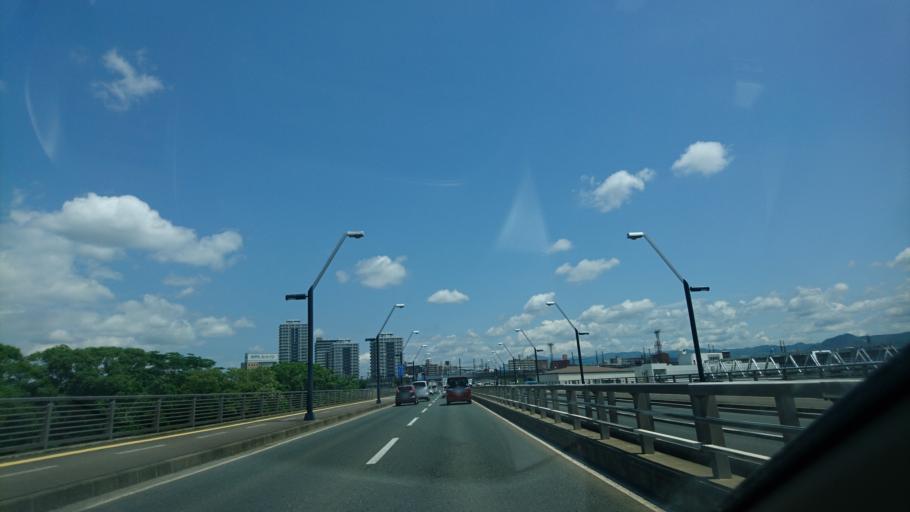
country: JP
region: Iwate
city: Morioka-shi
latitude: 39.6945
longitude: 141.1381
